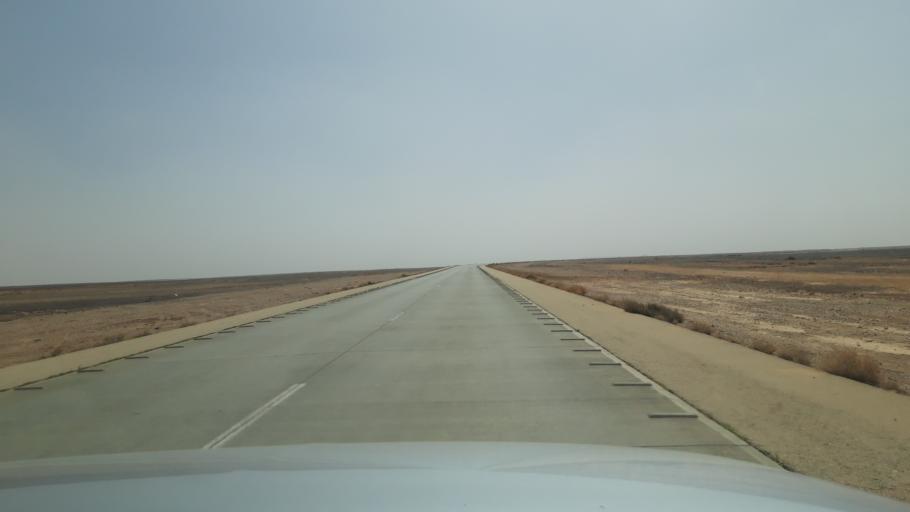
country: JO
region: Ma'an
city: Al Jafr
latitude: 30.9651
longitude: 36.6246
